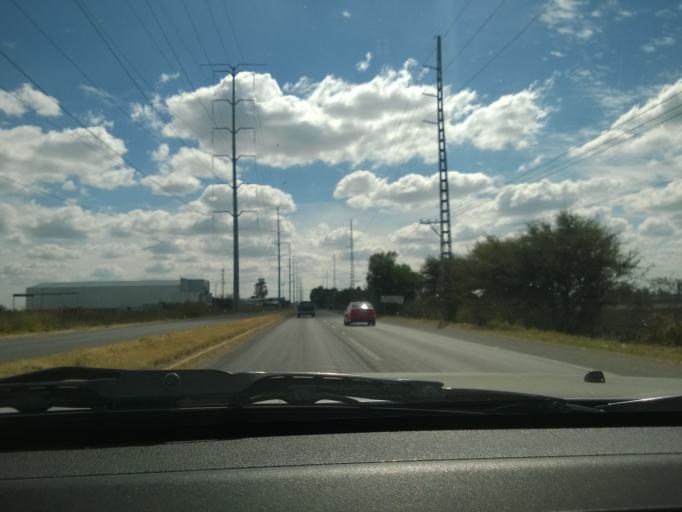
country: MX
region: Guanajuato
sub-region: Leon
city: Colonia Latinoamericana
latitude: 21.0385
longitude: -101.6931
